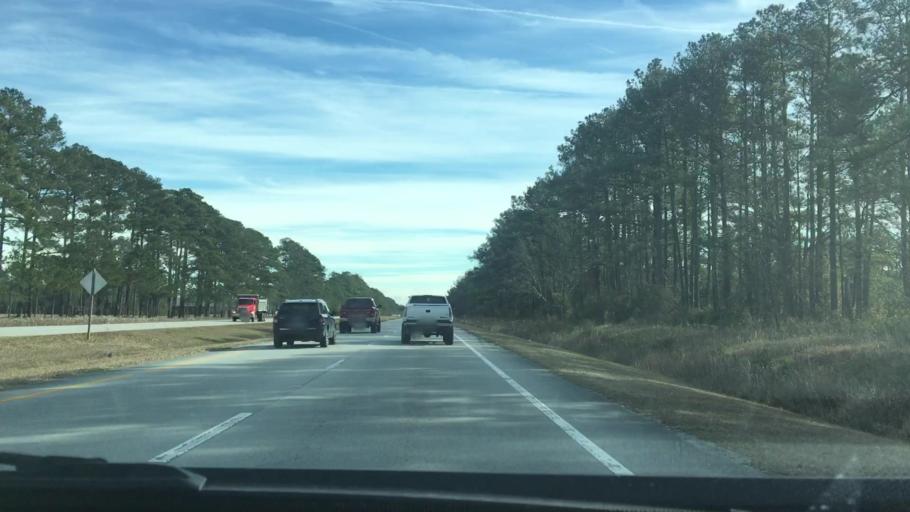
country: US
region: North Carolina
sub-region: Carteret County
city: Newport
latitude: 34.7689
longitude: -76.8632
